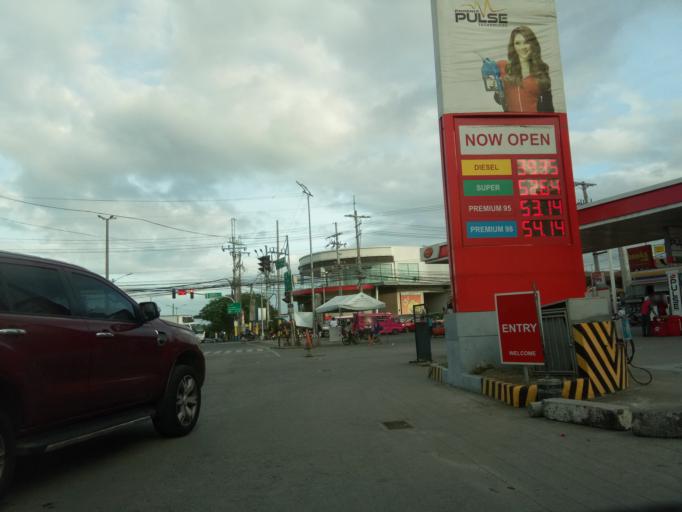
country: PH
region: Calabarzon
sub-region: Province of Cavite
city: Imus
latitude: 14.3860
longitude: 120.9775
